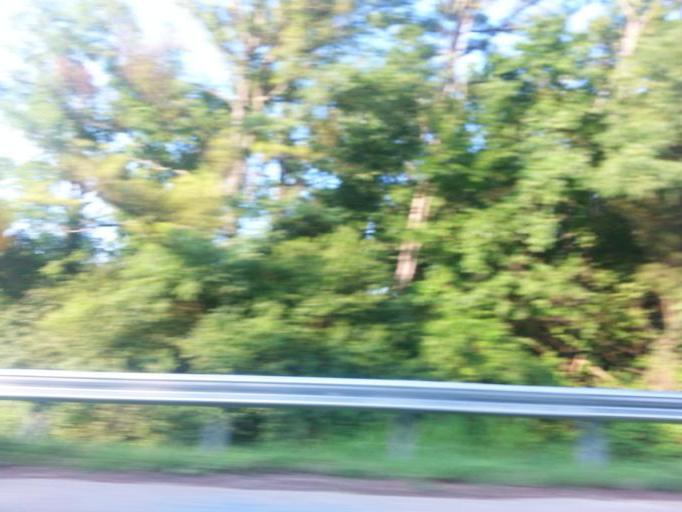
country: US
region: Tennessee
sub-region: Anderson County
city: Oak Ridge
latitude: 35.9785
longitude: -84.1788
